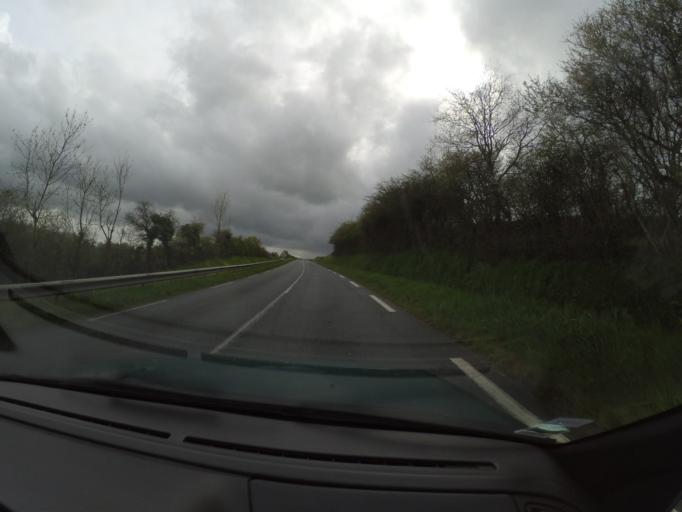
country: FR
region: Pays de la Loire
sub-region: Departement de la Loire-Atlantique
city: La Remaudiere
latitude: 47.2286
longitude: -1.2260
